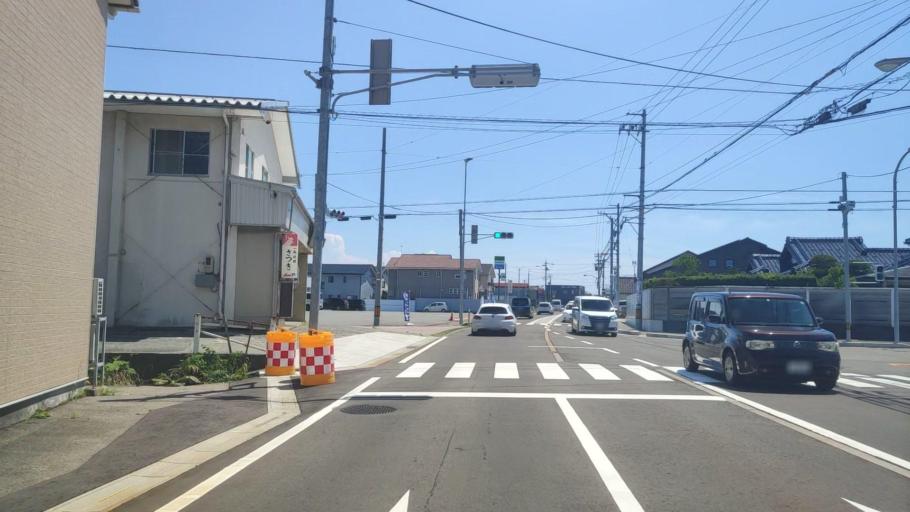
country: JP
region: Ishikawa
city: Kanazawa-shi
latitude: 36.6405
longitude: 136.6419
